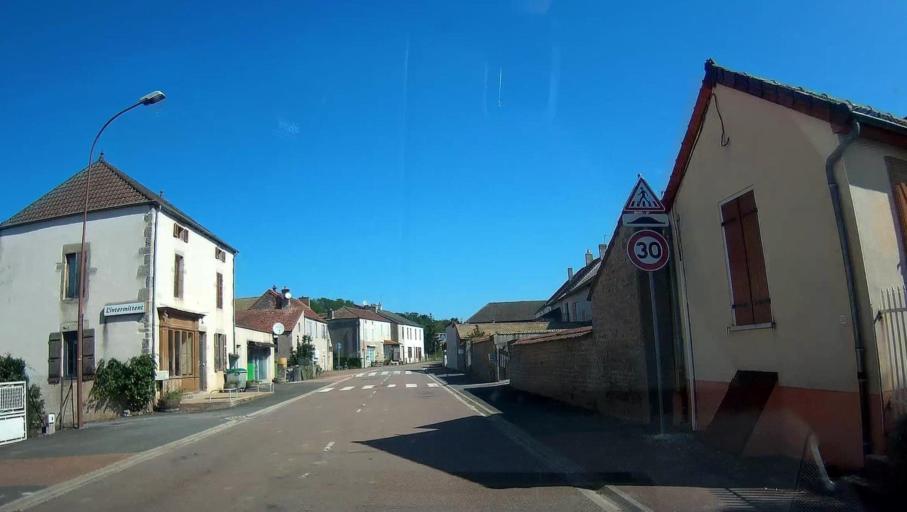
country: FR
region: Bourgogne
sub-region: Departement de Saone-et-Loire
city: Couches
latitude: 46.9093
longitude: 4.5960
